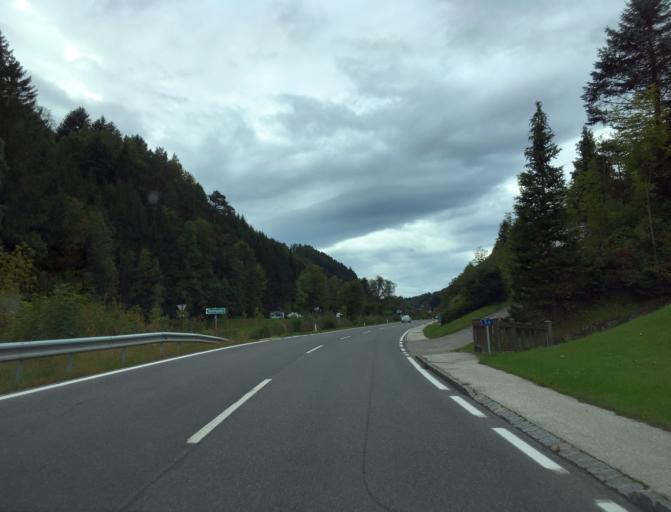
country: AT
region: Lower Austria
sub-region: Politischer Bezirk Neunkirchen
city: Thomasberg
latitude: 47.5746
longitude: 16.1430
